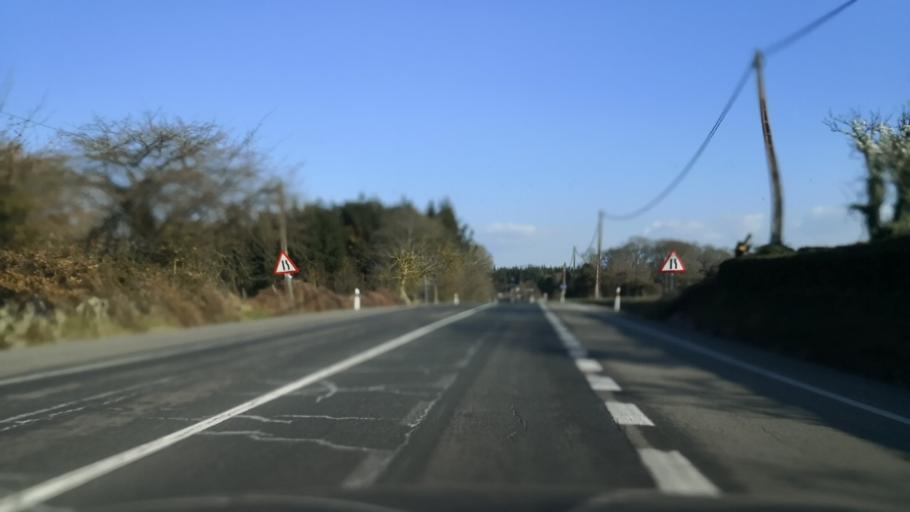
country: ES
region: Galicia
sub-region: Provincia de Lugo
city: Corgo
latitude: 42.9543
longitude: -7.4641
